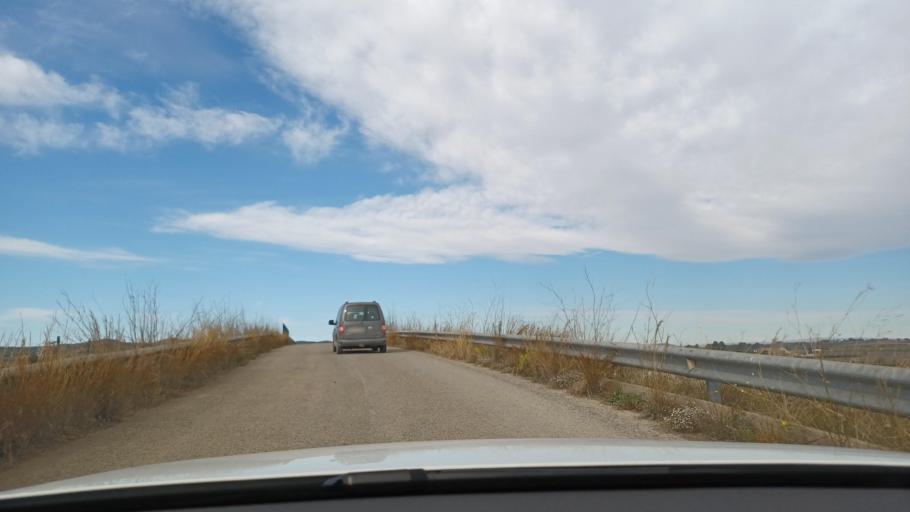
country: ES
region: Valencia
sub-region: Provincia de Valencia
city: Benifaio
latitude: 39.2913
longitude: -0.4362
